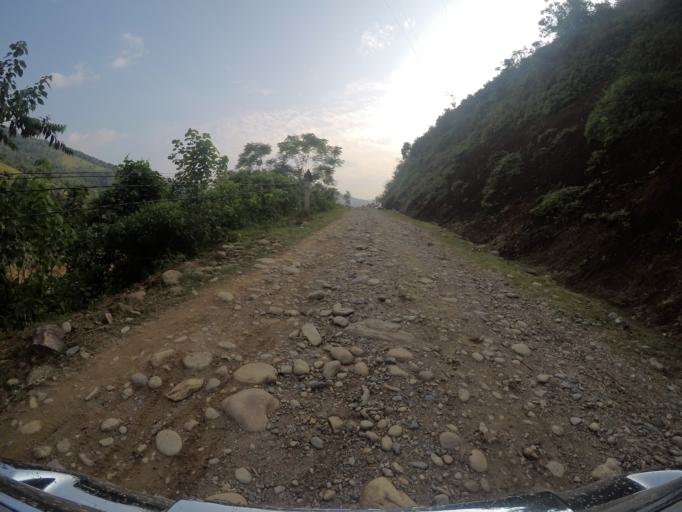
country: VN
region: Yen Bai
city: Son Thinh
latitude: 21.6895
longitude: 104.6303
